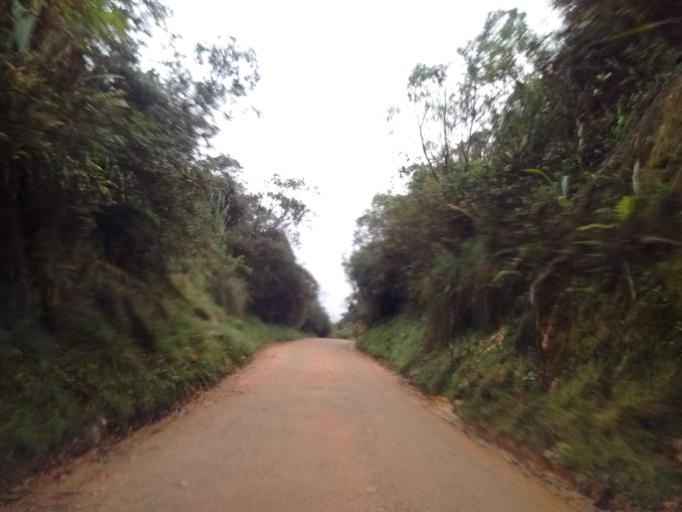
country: CO
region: Huila
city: Isnos
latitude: 2.1166
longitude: -76.3754
